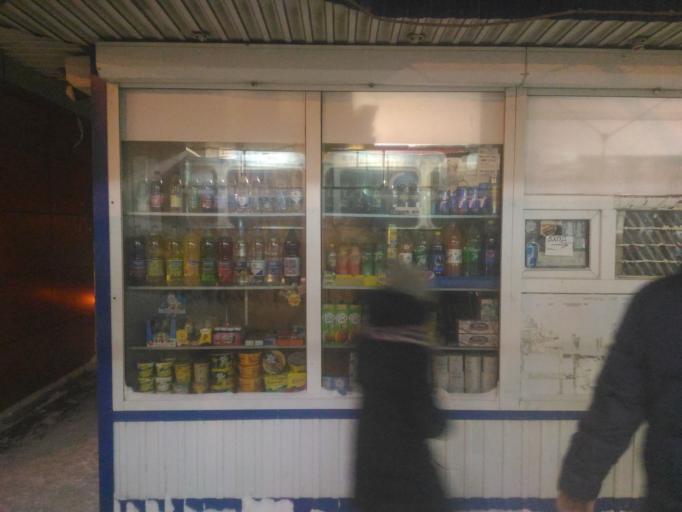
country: RU
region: Ulyanovsk
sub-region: Ulyanovskiy Rayon
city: Ulyanovsk
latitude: 54.3151
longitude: 48.3562
